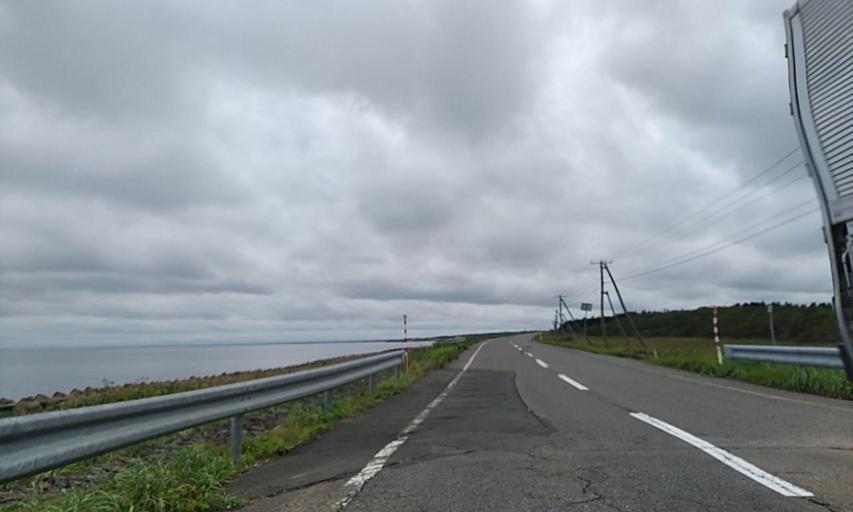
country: JP
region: Hokkaido
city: Shibetsu
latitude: 43.4442
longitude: 145.2620
